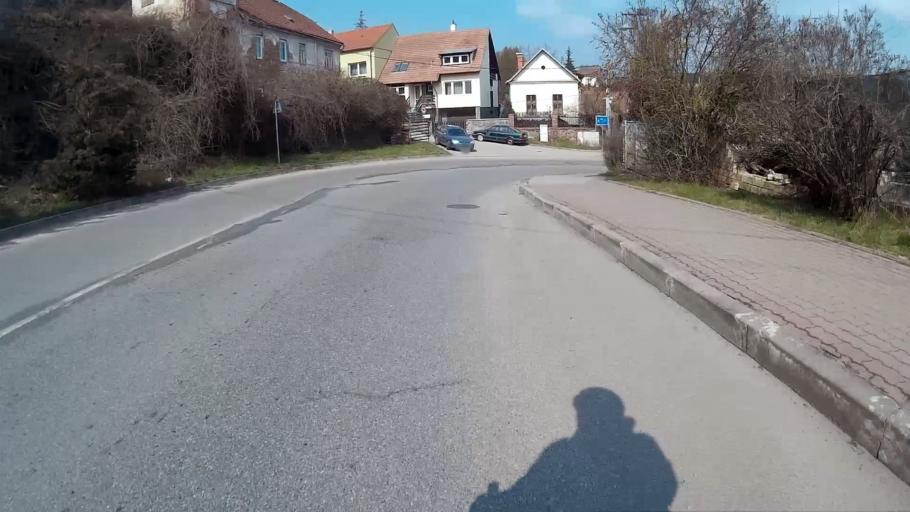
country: CZ
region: South Moravian
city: Bilovice nad Svitavou
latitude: 49.2468
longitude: 16.6717
